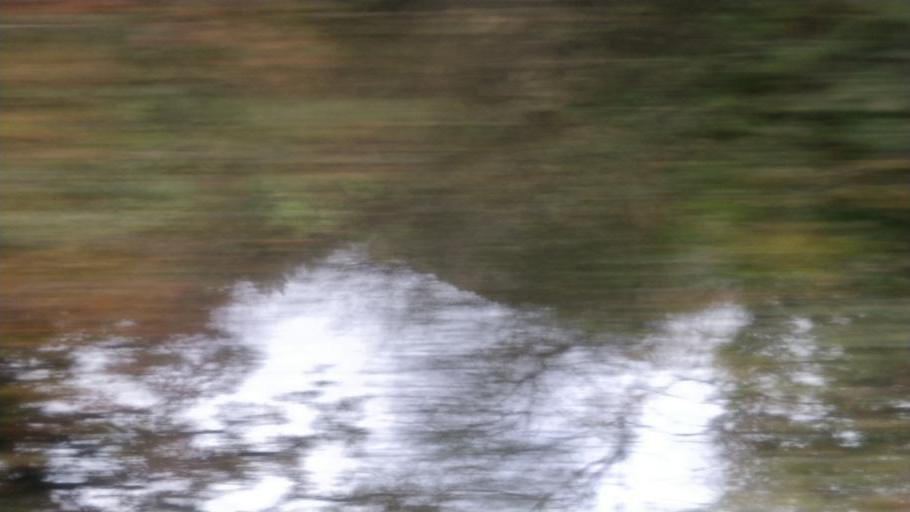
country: GB
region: England
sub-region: Lancashire
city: Appley Bridge
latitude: 53.5674
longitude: -2.7097
